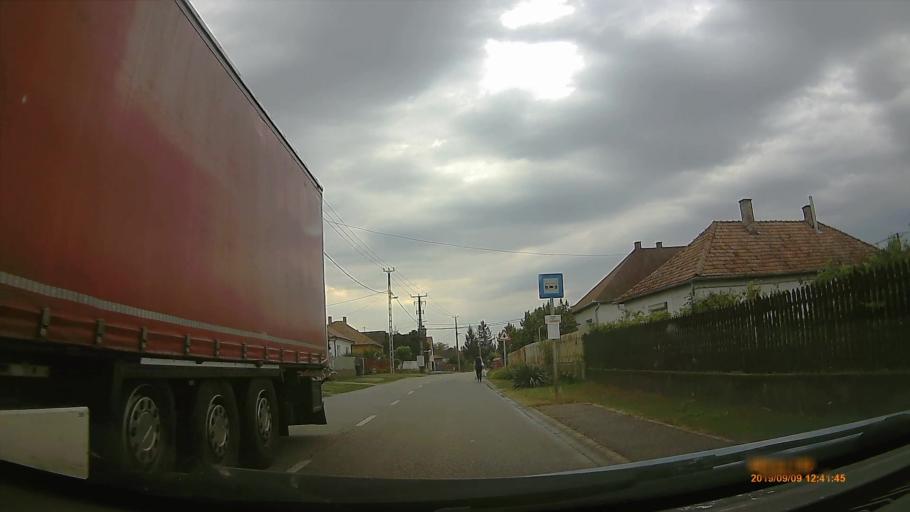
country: HU
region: Szabolcs-Szatmar-Bereg
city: Nyirpazony
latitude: 47.9780
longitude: 21.8019
